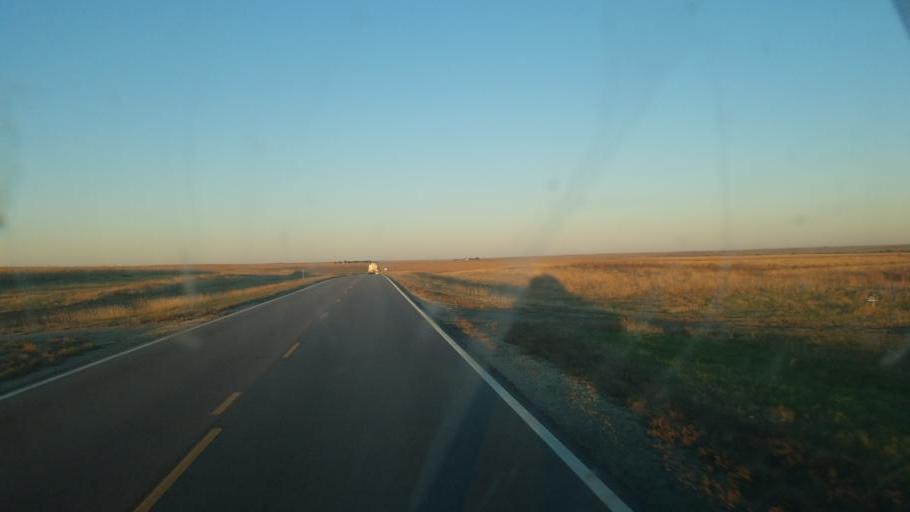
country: US
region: Kansas
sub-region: Wallace County
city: Sharon Springs
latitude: 38.9012
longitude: -101.8520
